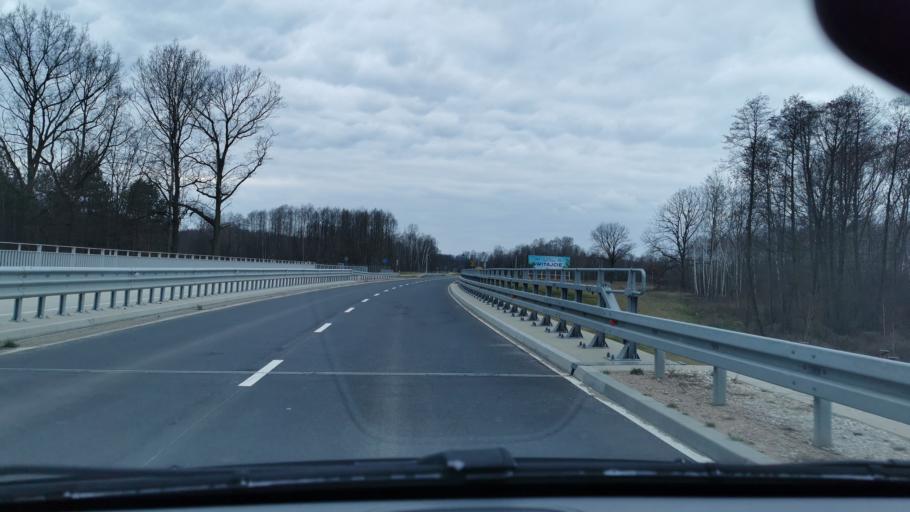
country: PL
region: Masovian Voivodeship
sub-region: Powiat zyrardowski
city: Zyrardow
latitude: 52.0119
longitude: 20.4739
